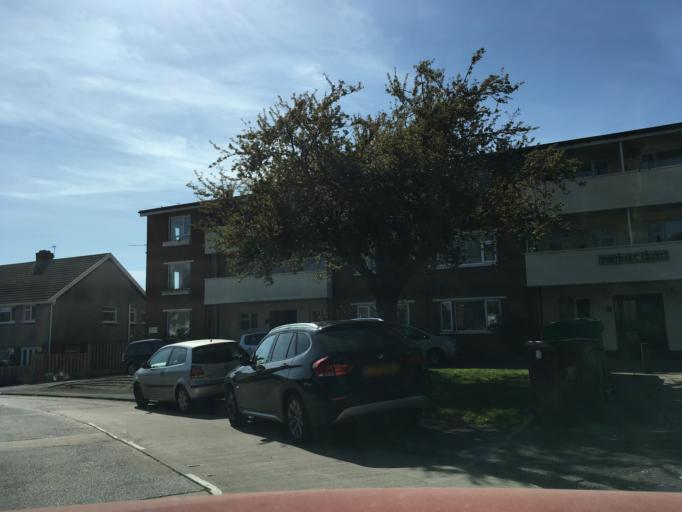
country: GB
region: Wales
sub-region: Cardiff
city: Radyr
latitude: 51.5268
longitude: -3.2302
